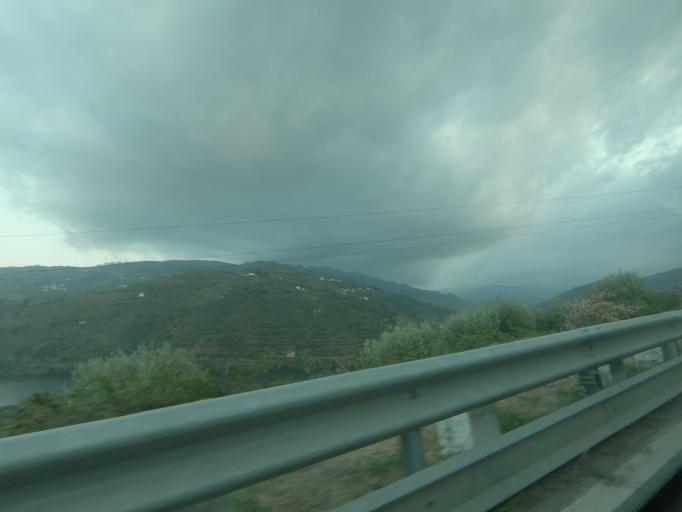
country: PT
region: Vila Real
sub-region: Mesao Frio
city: Mesao Frio
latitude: 41.1626
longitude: -7.8712
